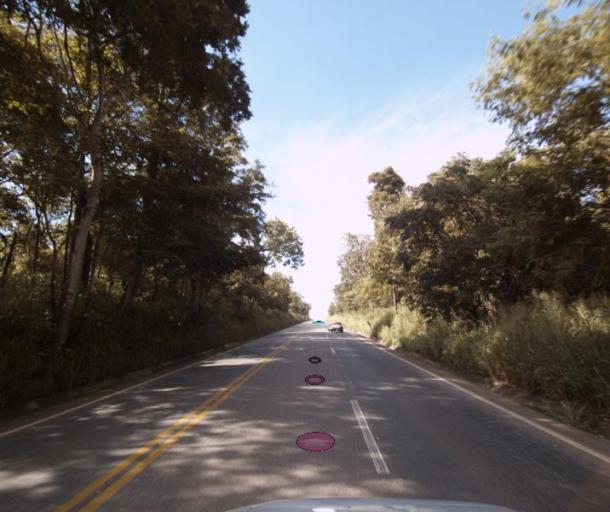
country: BR
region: Goias
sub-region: Porangatu
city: Porangatu
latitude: -13.0908
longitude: -49.1940
